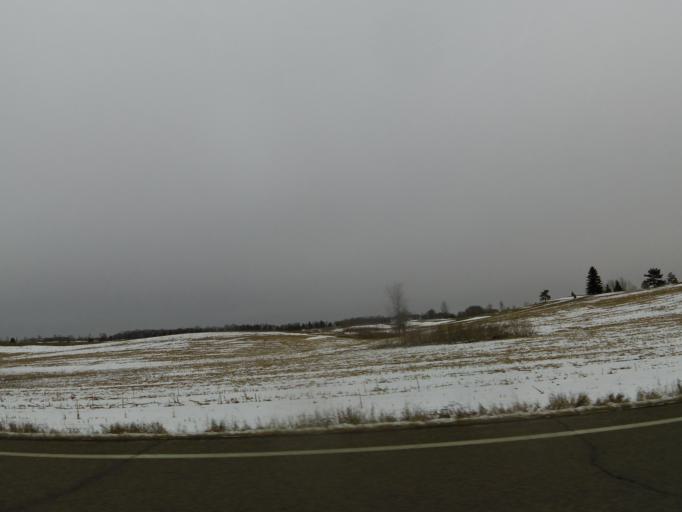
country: US
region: Minnesota
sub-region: Scott County
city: Jordan
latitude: 44.6307
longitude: -93.6077
